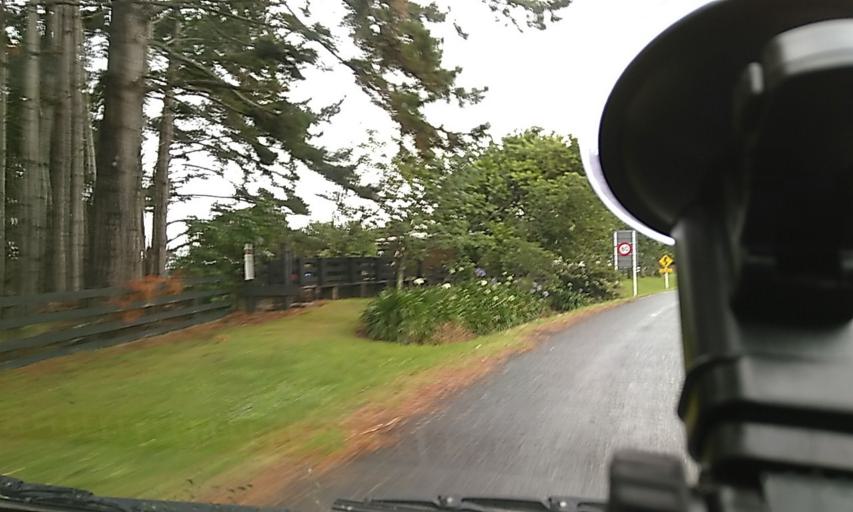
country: NZ
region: Auckland
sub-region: Auckland
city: Pukekohe East
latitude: -37.3241
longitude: 174.9180
